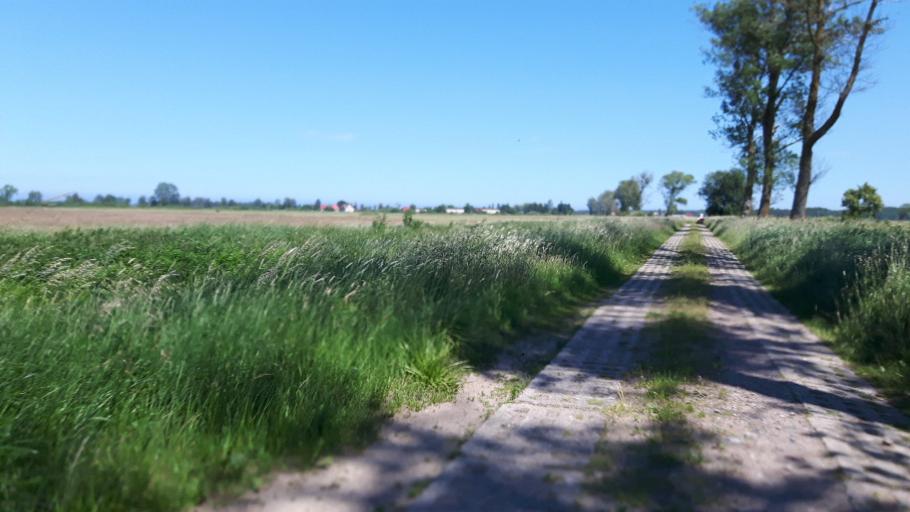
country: PL
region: Pomeranian Voivodeship
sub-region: Powiat slupski
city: Smoldzino
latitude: 54.6791
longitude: 17.2710
